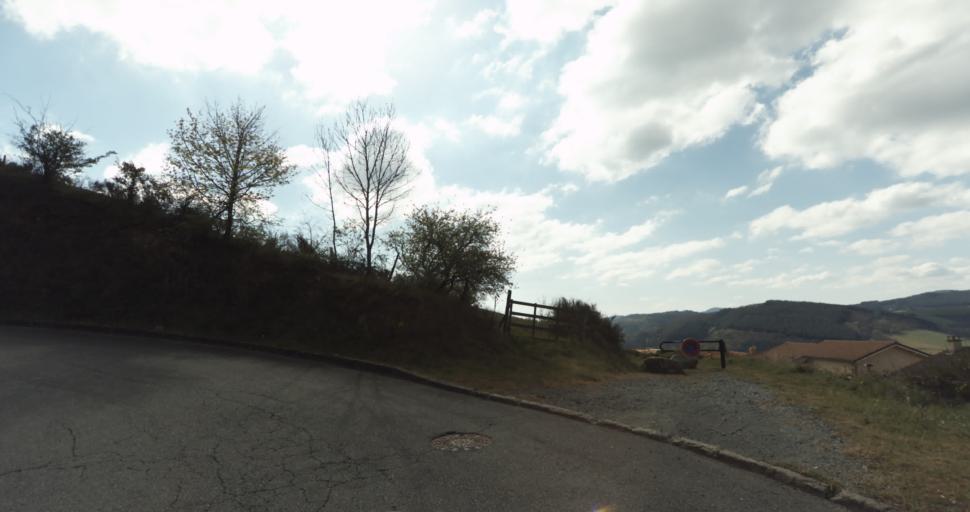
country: FR
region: Rhone-Alpes
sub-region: Departement du Rhone
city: Tarare
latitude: 45.8983
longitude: 4.4458
